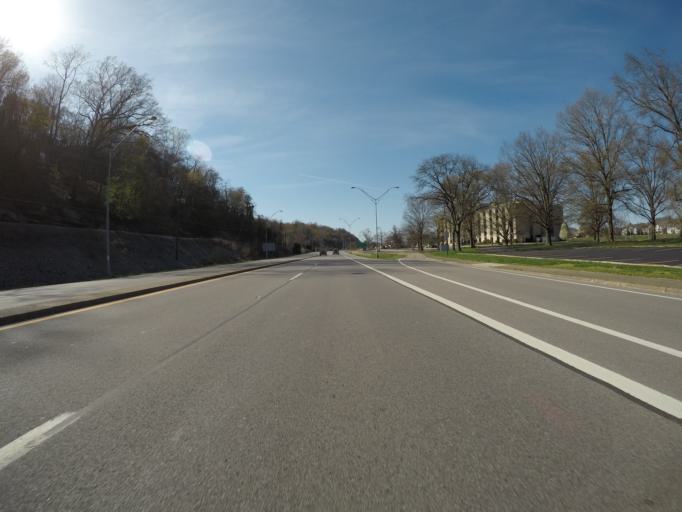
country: US
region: West Virginia
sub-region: Kanawha County
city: Charleston
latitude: 38.3359
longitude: -81.6257
